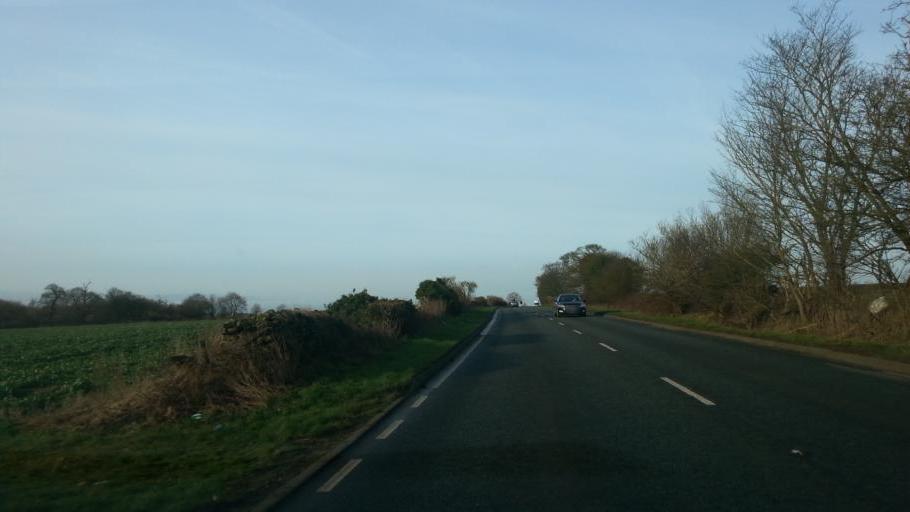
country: GB
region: England
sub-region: Leicestershire
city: Wymondham
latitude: 52.8451
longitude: -0.7879
